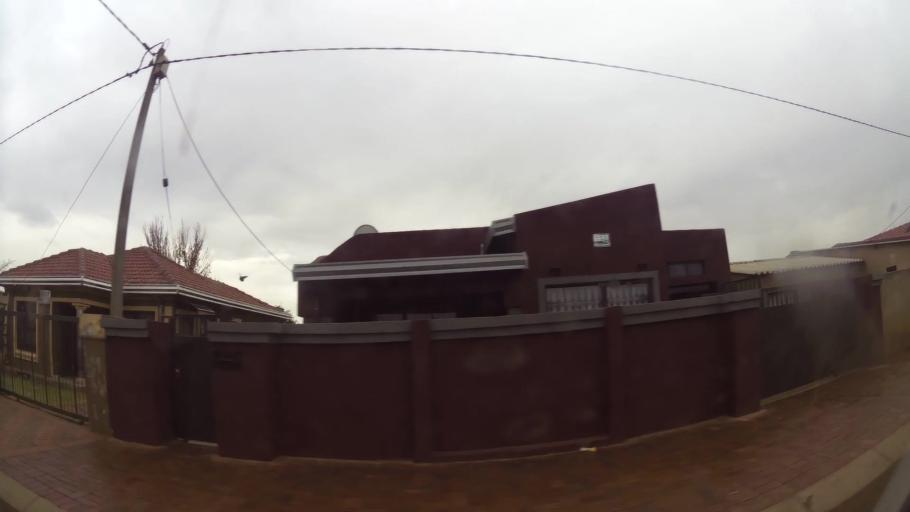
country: ZA
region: Gauteng
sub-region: Ekurhuleni Metropolitan Municipality
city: Germiston
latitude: -26.3774
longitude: 28.1763
